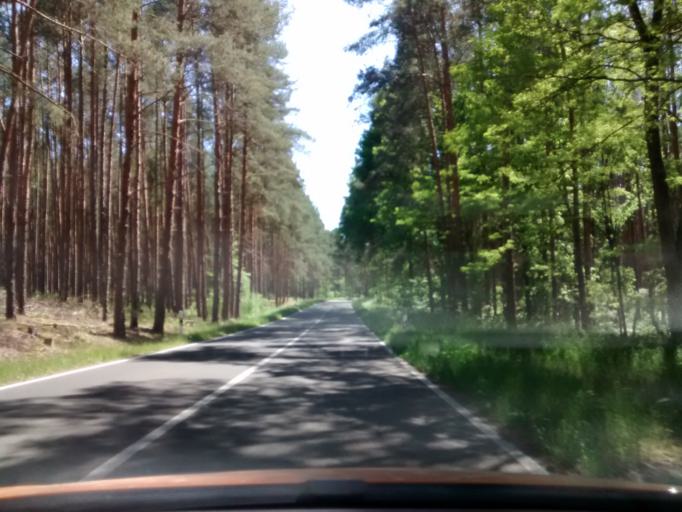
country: DE
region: Brandenburg
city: Wendisch Rietz
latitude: 52.2275
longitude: 13.9992
